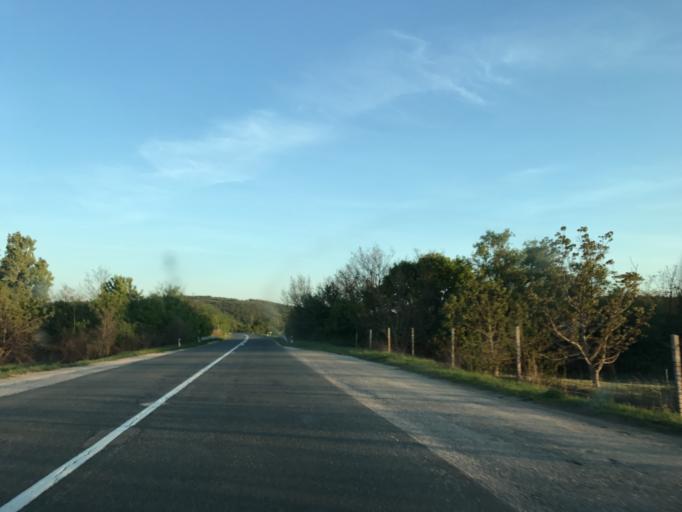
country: RO
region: Mehedinti
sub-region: Comuna Gogosu
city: Ostrovu Mare
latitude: 44.4382
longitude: 22.4582
